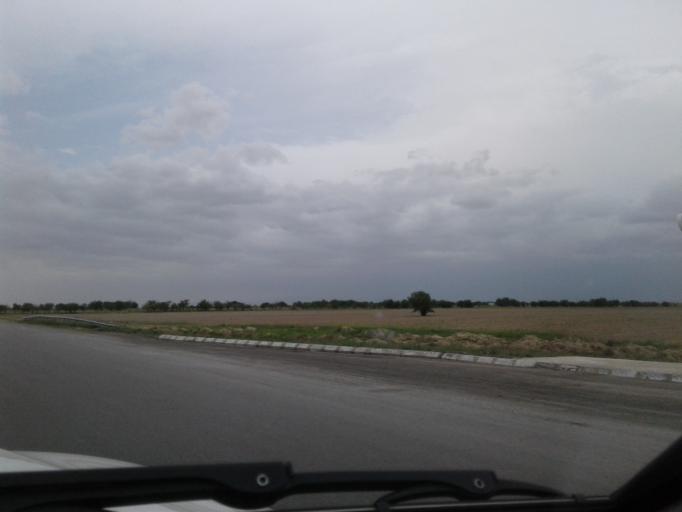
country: TM
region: Ahal
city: Kaka
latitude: 37.4813
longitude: 59.4816
